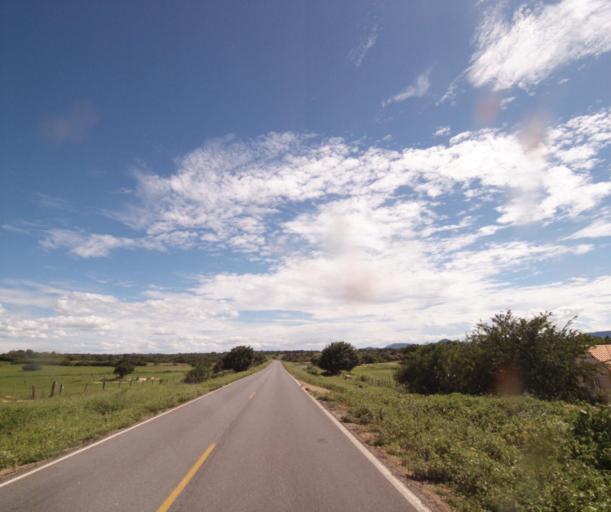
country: BR
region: Bahia
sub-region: Guanambi
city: Guanambi
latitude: -14.5567
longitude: -42.7020
